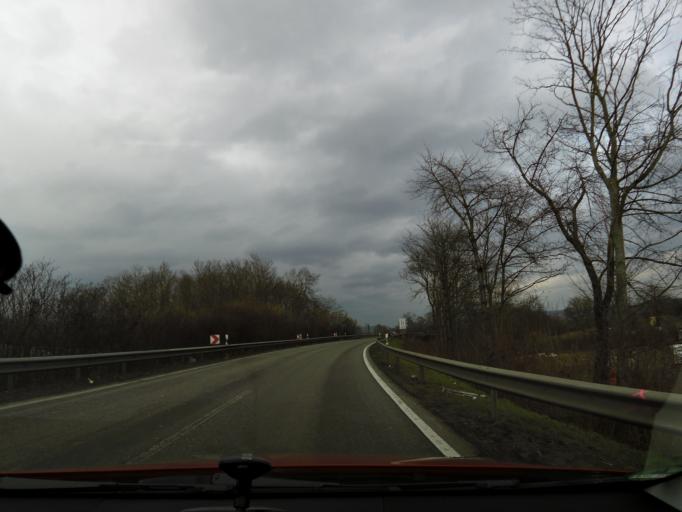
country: DE
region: Rheinland-Pfalz
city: Kaltenengers
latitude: 50.3925
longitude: 7.5473
